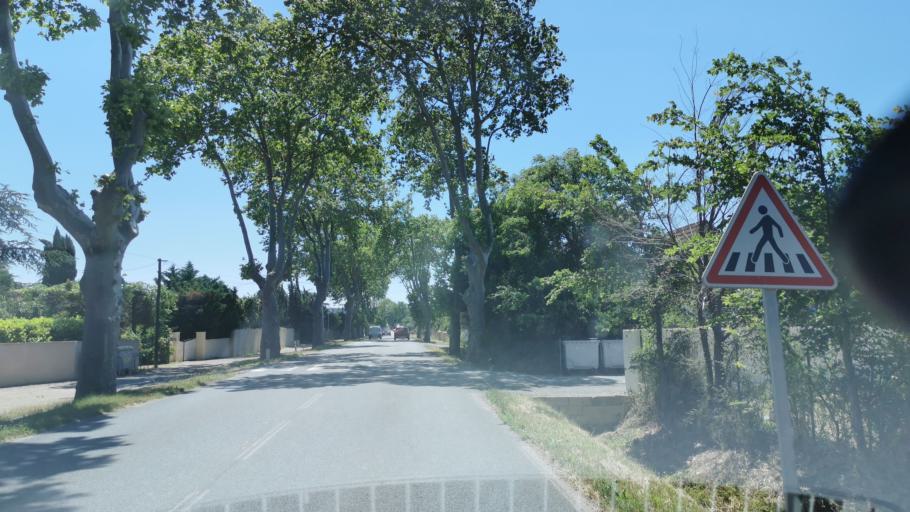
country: FR
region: Languedoc-Roussillon
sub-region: Departement de l'Aude
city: Saint-Marcel-sur-Aude
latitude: 43.2498
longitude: 2.9162
